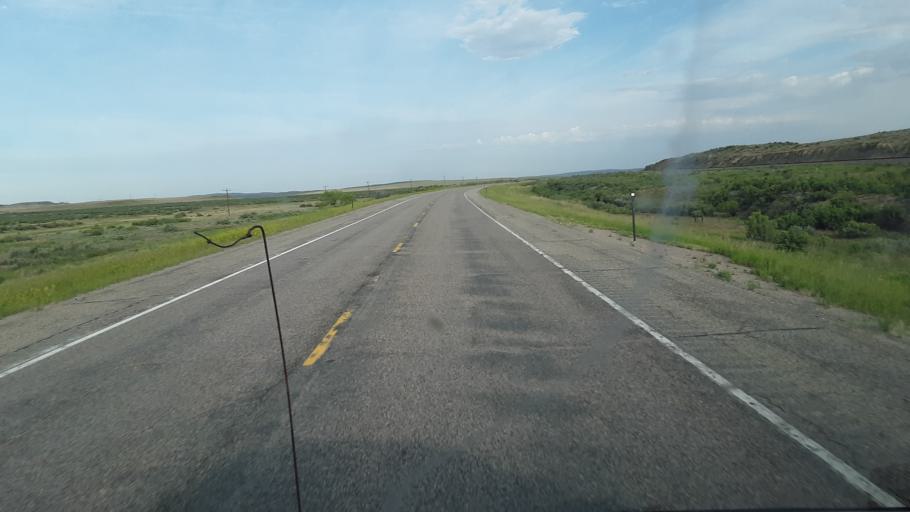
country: US
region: Wyoming
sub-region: Natrona County
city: Bar Nunn
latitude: 43.0299
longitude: -106.8244
